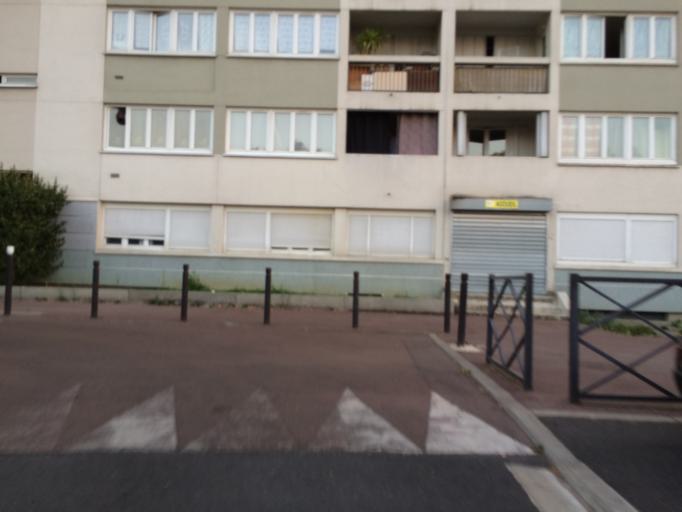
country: FR
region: Ile-de-France
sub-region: Departement de l'Essonne
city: Massy
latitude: 48.7387
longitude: 2.2890
